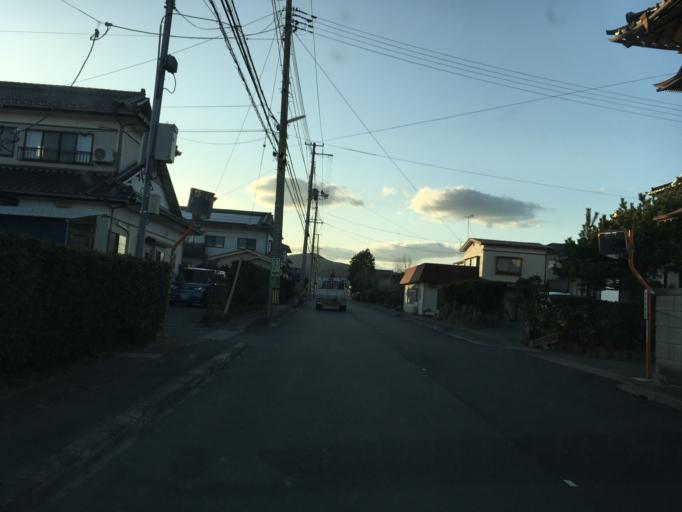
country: JP
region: Iwate
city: Ofunato
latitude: 38.8336
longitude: 141.5822
